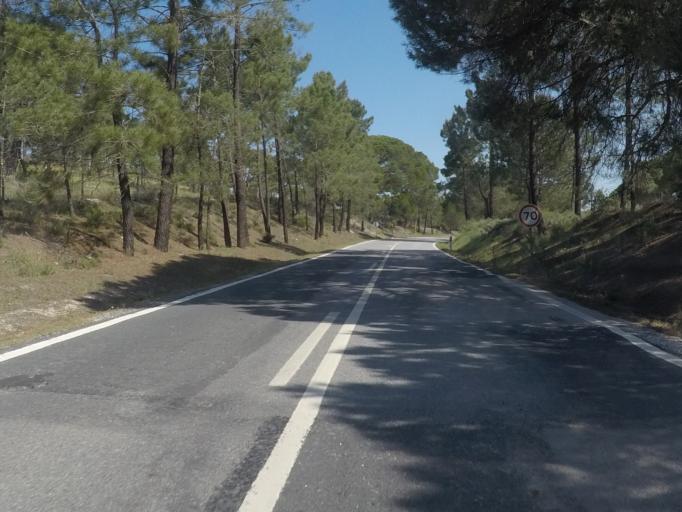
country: PT
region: Setubal
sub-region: Grandola
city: Grandola
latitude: 38.2947
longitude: -8.7267
